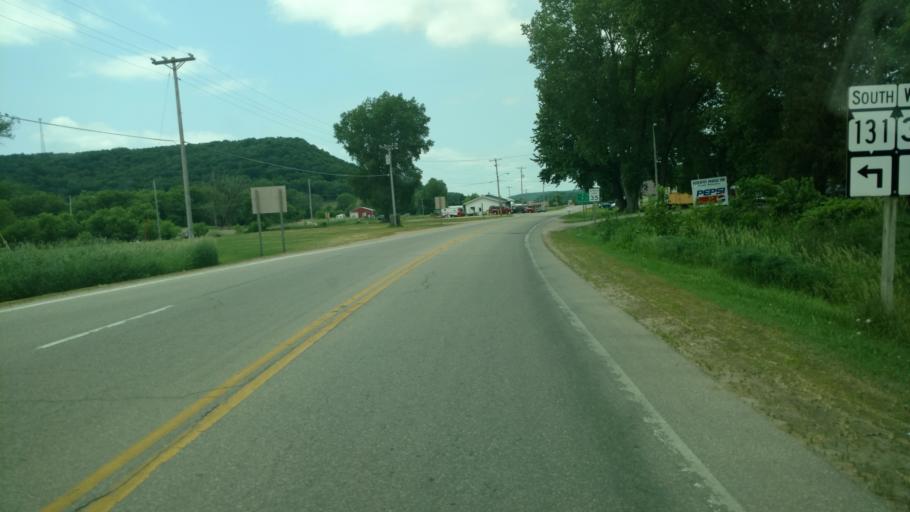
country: US
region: Wisconsin
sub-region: Monroe County
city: Cashton
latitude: 43.7220
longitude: -90.5902
